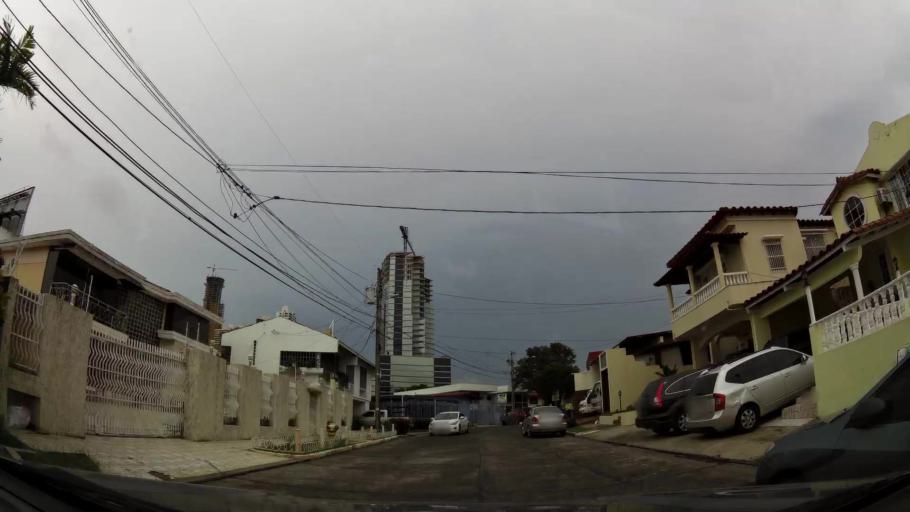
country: PA
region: Panama
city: Panama
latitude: 8.9986
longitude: -79.5325
